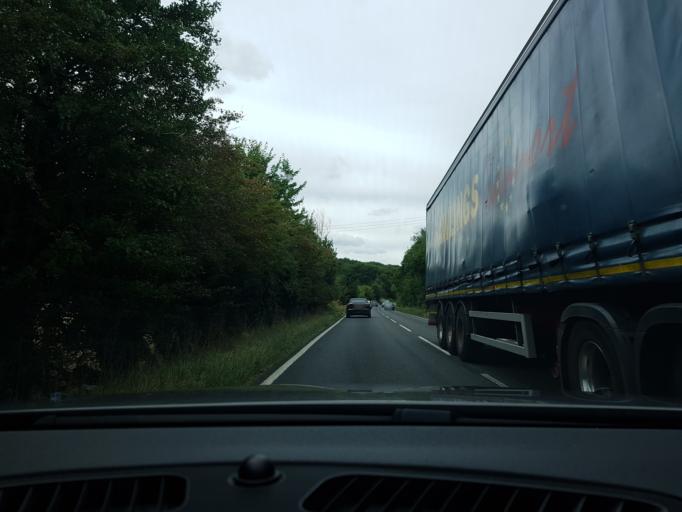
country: GB
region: England
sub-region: Hampshire
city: Kingsclere
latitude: 51.3211
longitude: -1.2167
